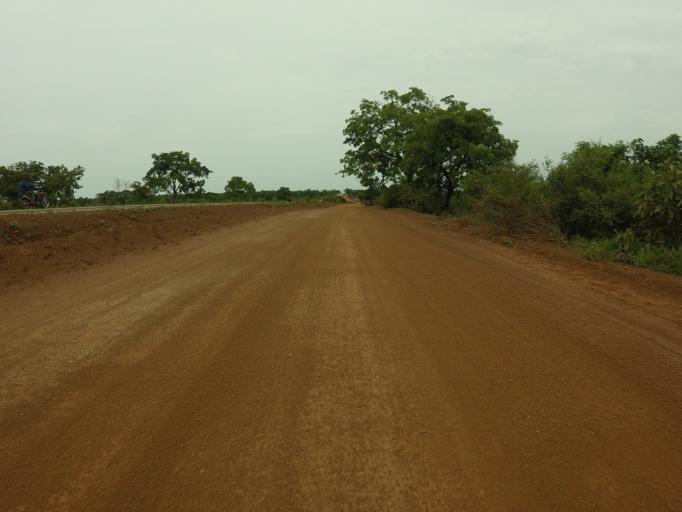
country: GH
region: Northern
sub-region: Yendi
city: Yendi
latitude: 9.0250
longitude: -0.0138
